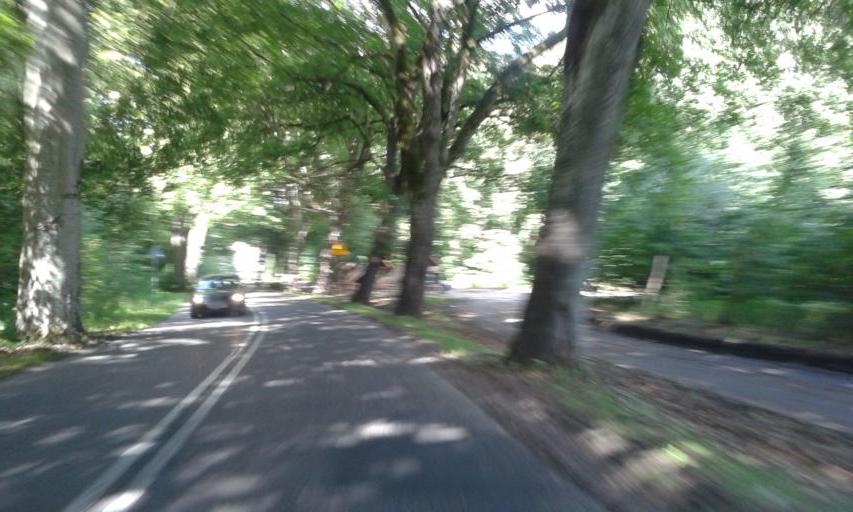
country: PL
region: West Pomeranian Voivodeship
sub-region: Powiat slawienski
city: Slawno
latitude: 54.2539
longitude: 16.6848
